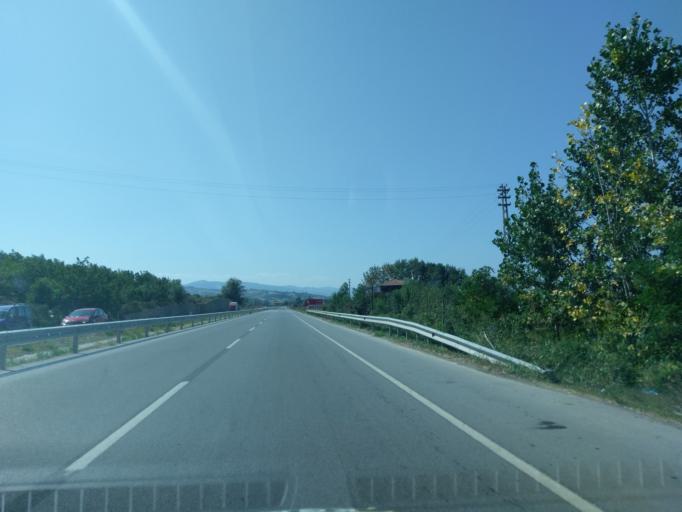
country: TR
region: Samsun
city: Alacam
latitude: 41.6084
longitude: 35.6741
